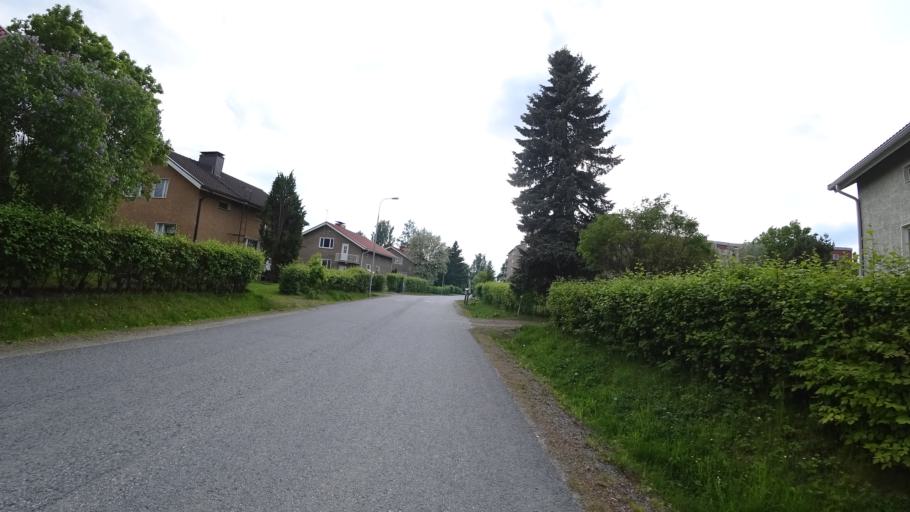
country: FI
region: Pirkanmaa
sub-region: Tampere
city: Pirkkala
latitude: 61.4974
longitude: 23.6422
